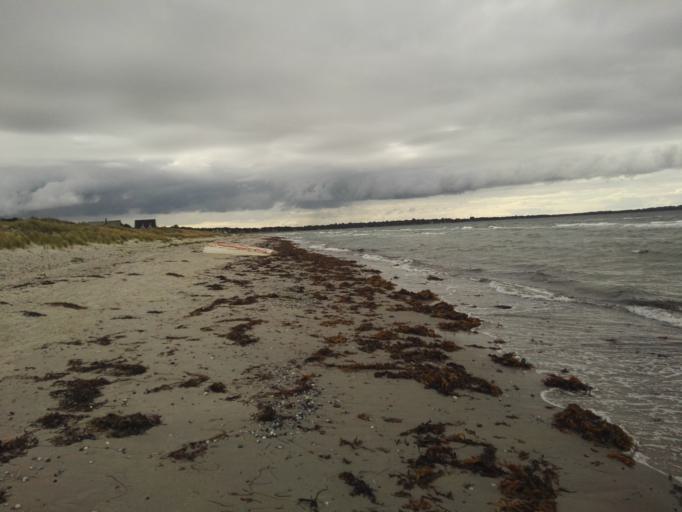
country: DK
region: Zealand
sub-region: Odsherred Kommune
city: Nykobing Sjaelland
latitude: 55.9440
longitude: 11.6707
